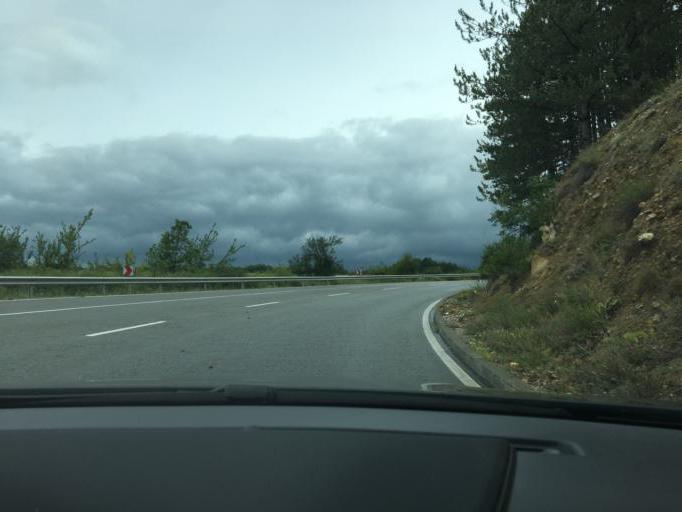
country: BG
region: Kyustendil
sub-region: Obshtina Bobovdol
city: Bobovdol
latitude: 42.2671
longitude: 22.9563
